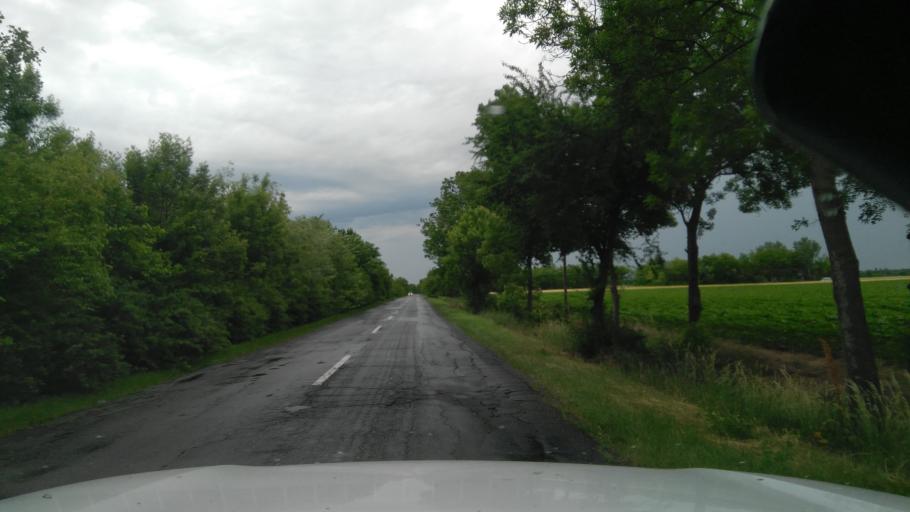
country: HU
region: Bekes
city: Bekescsaba
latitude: 46.6863
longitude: 21.1669
